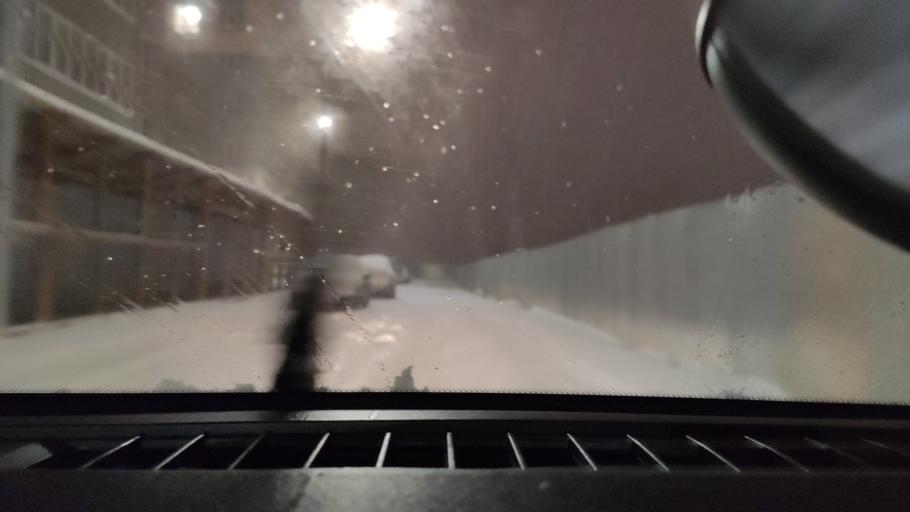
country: RU
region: Samara
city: Samara
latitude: 53.1057
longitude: 50.1387
